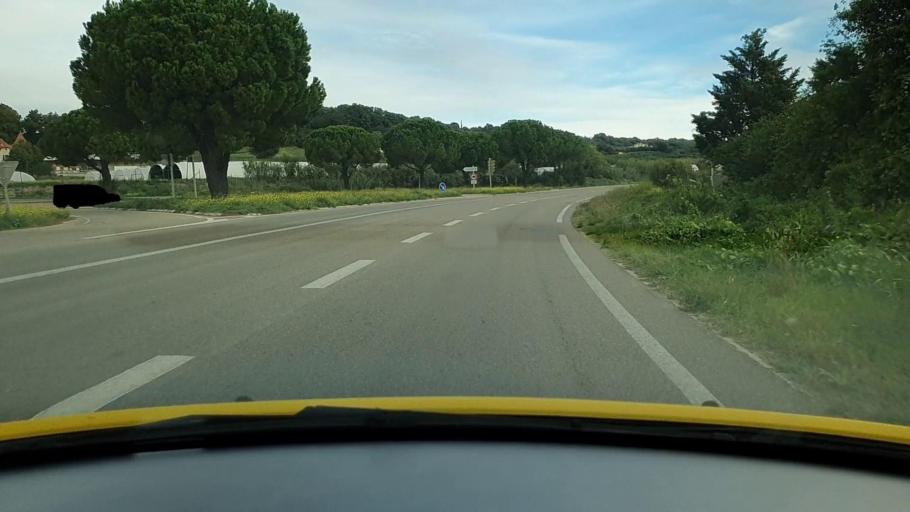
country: FR
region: Languedoc-Roussillon
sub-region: Departement du Gard
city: Bellegarde
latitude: 43.7612
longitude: 4.5249
